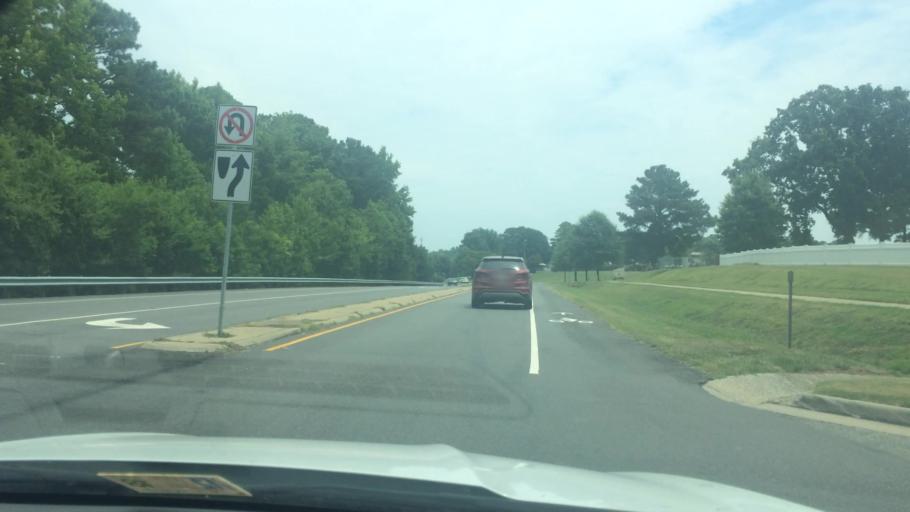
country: US
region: Virginia
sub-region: James City County
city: Williamsburg
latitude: 37.2679
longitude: -76.7636
